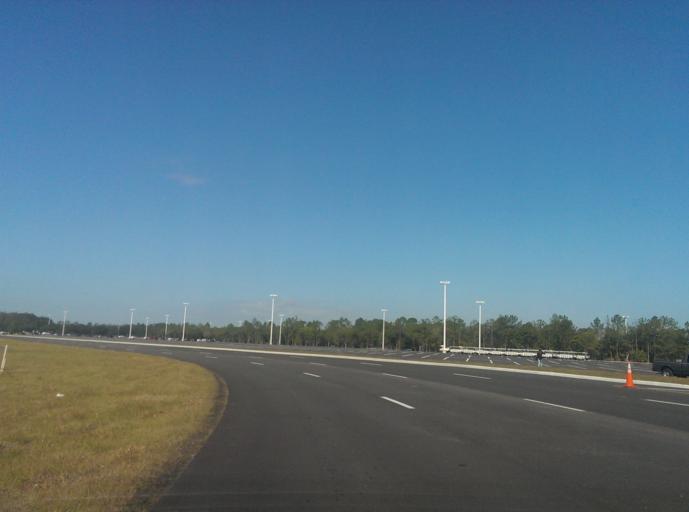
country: US
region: Florida
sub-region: Osceola County
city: Celebration
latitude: 28.3973
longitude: -81.5755
